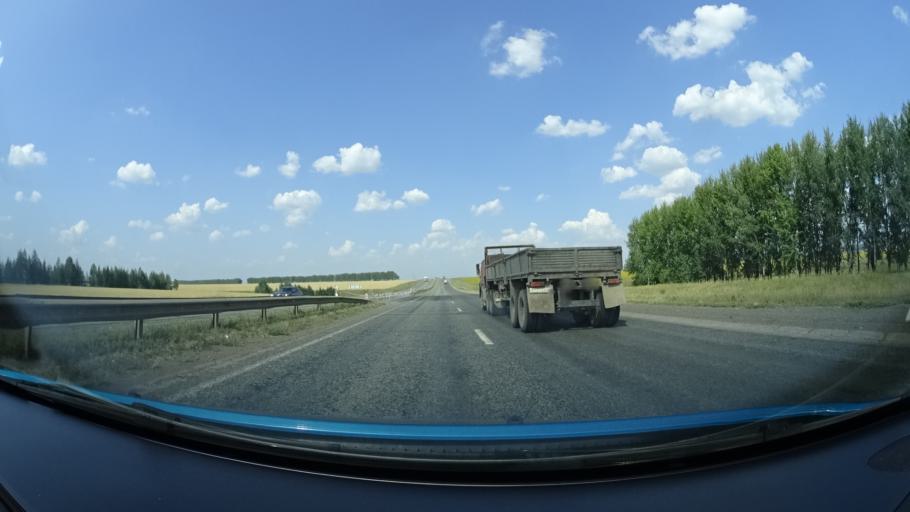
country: RU
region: Bashkortostan
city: Dmitriyevka
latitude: 54.6809
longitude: 55.3332
